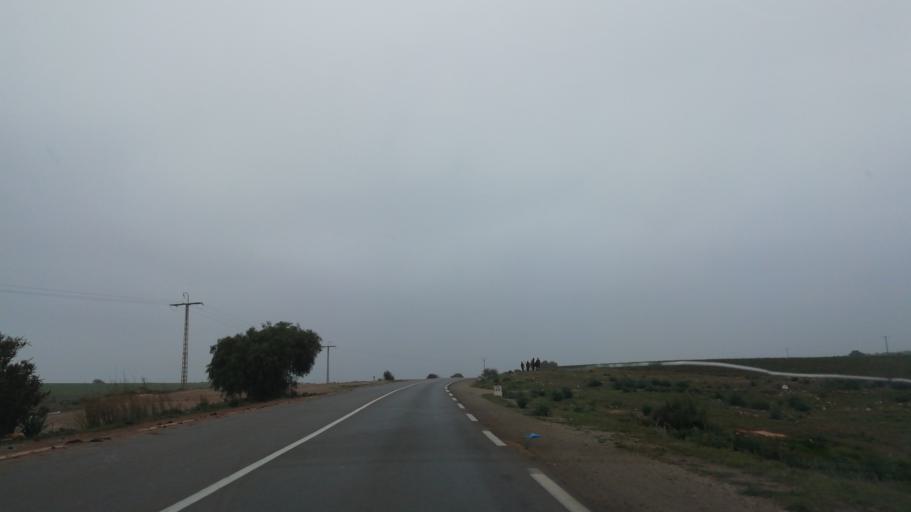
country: DZ
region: Mascara
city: Mascara
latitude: 35.3080
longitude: 0.4162
